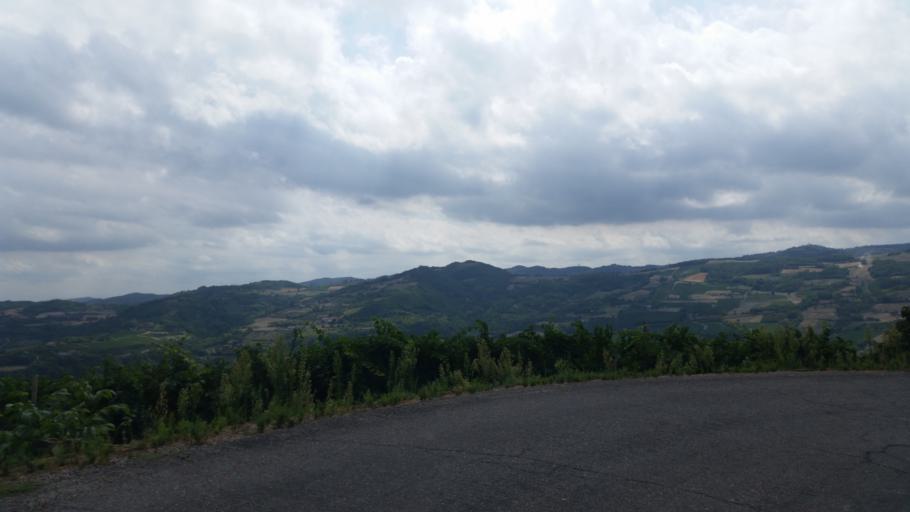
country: IT
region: Piedmont
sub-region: Provincia di Asti
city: Vesime
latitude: 44.6458
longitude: 8.2309
